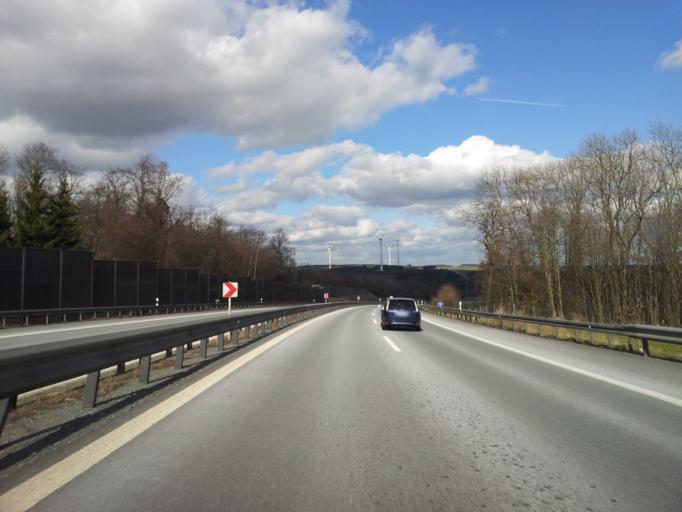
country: DE
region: Bavaria
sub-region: Upper Franconia
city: Koditz
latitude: 50.3478
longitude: 11.8494
